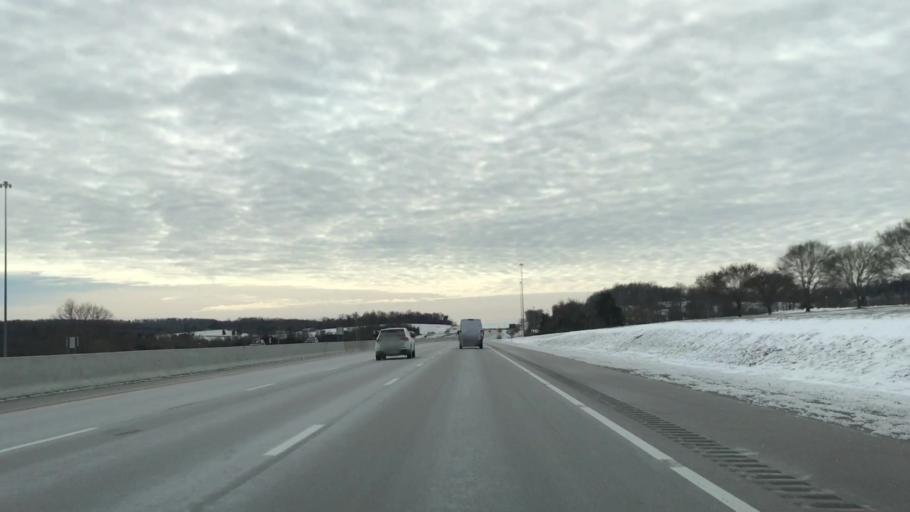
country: US
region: Kentucky
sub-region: Hart County
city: Munfordville
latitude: 37.2374
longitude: -85.9288
